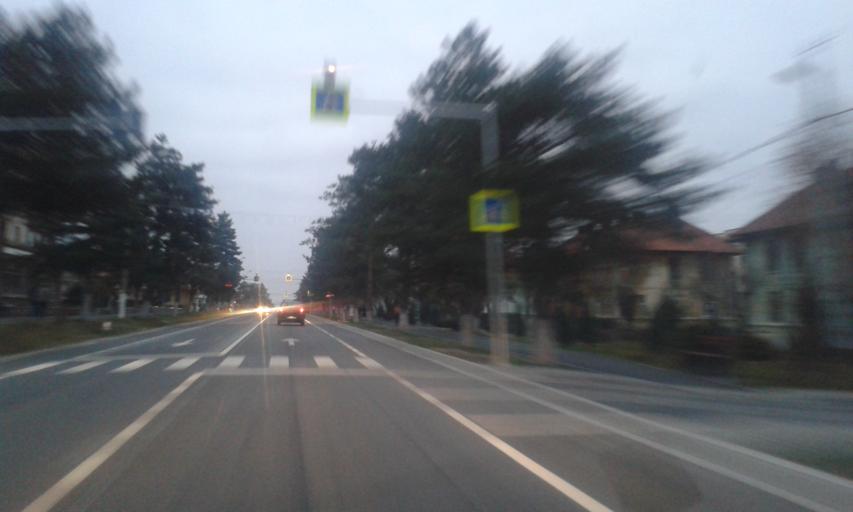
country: RO
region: Gorj
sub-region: Comuna Bumbesti-Jiu
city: Bumbesti-Jiu
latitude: 45.1793
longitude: 23.3799
